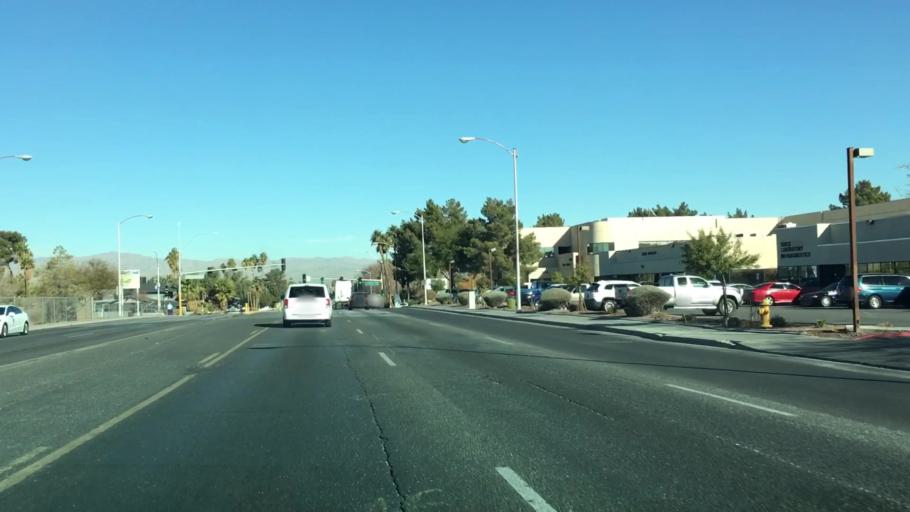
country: US
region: Nevada
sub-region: Clark County
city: Winchester
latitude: 36.1172
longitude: -115.1190
